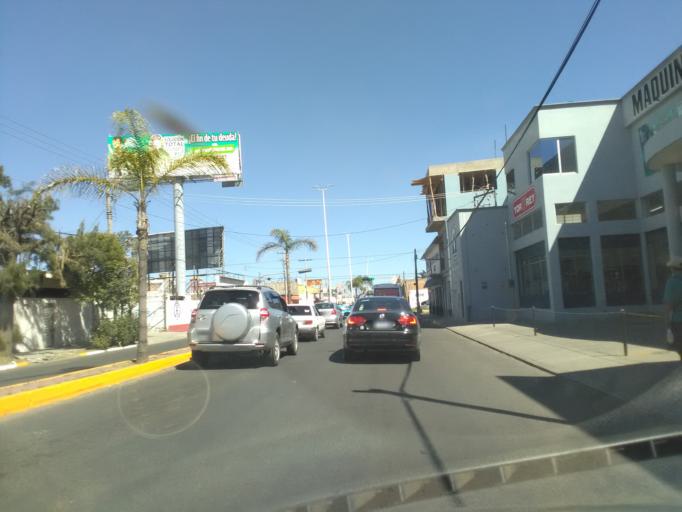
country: MX
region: Durango
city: Victoria de Durango
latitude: 24.0199
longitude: -104.6525
